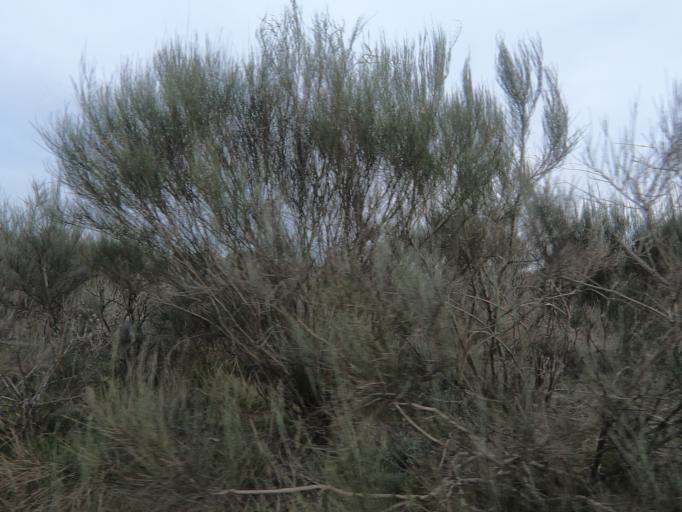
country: PT
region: Vila Real
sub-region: Sabrosa
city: Sabrosa
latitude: 41.3203
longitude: -7.6280
